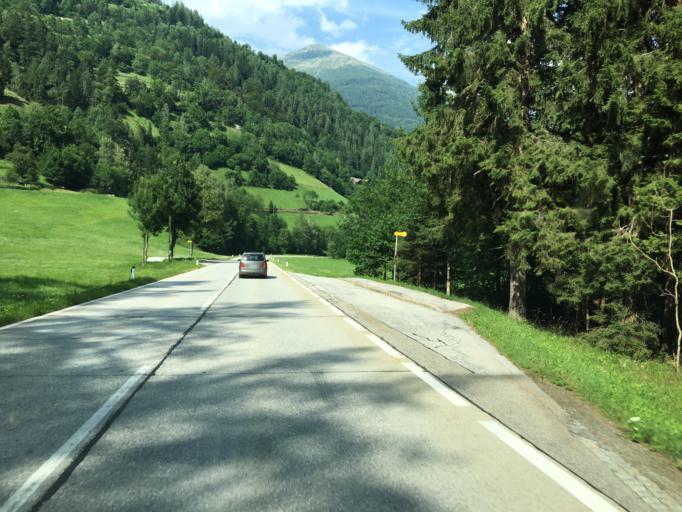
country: AT
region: Carinthia
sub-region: Politischer Bezirk Spittal an der Drau
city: Flattach
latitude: 46.9317
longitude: 13.0860
